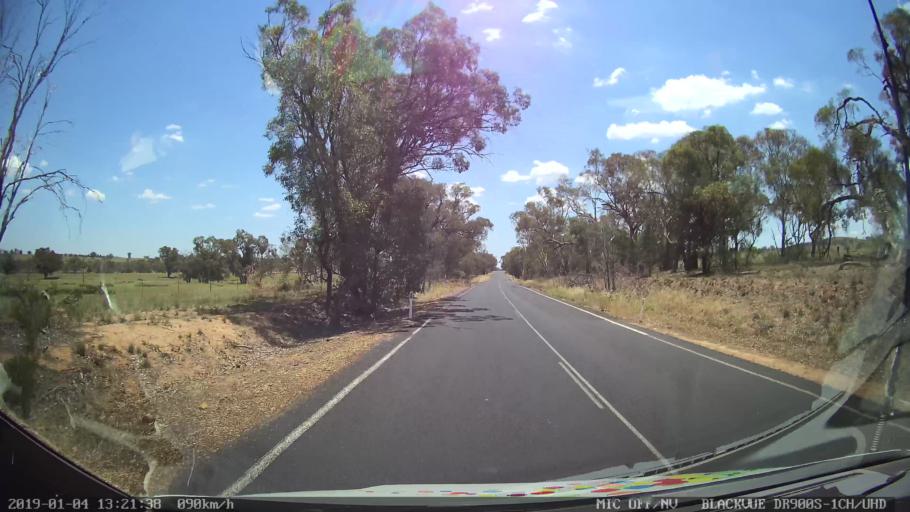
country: AU
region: New South Wales
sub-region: Parkes
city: Peak Hill
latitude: -32.7355
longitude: 148.5748
